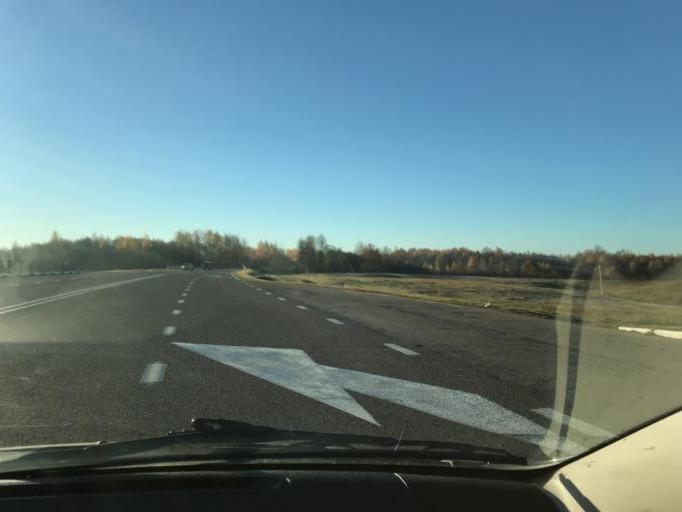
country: BY
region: Vitebsk
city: Vitebsk
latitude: 55.0890
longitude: 30.3076
